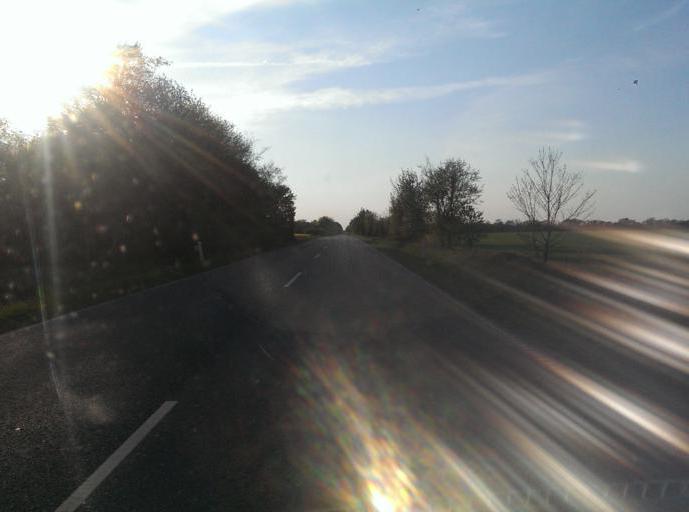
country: DK
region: South Denmark
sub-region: Esbjerg Kommune
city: Tjaereborg
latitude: 55.4919
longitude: 8.5867
